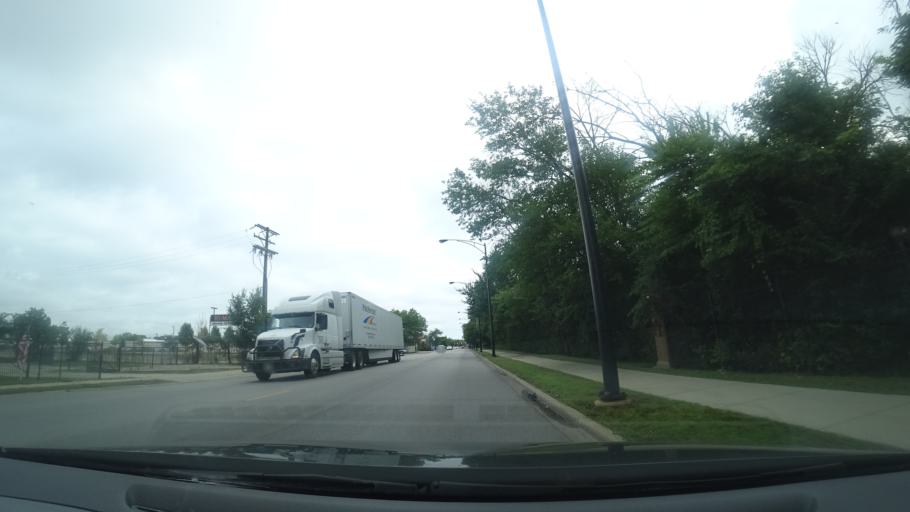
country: US
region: Illinois
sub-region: Cook County
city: Lincolnwood
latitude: 41.9866
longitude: -87.7285
